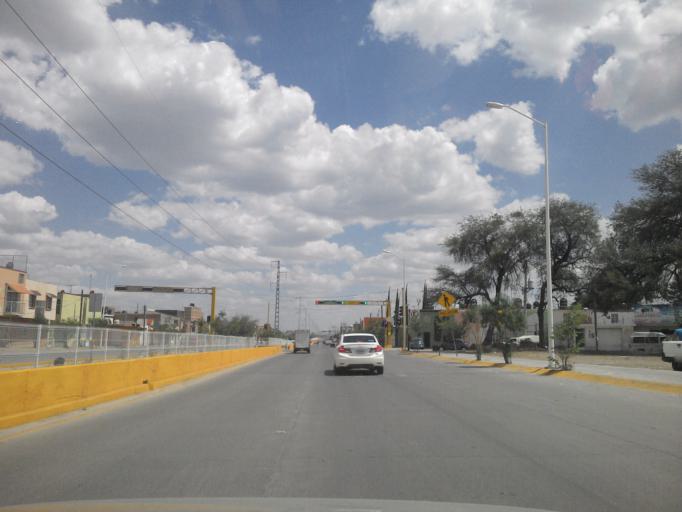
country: MX
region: Guanajuato
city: San Francisco del Rincon
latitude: 21.0281
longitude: -101.8694
